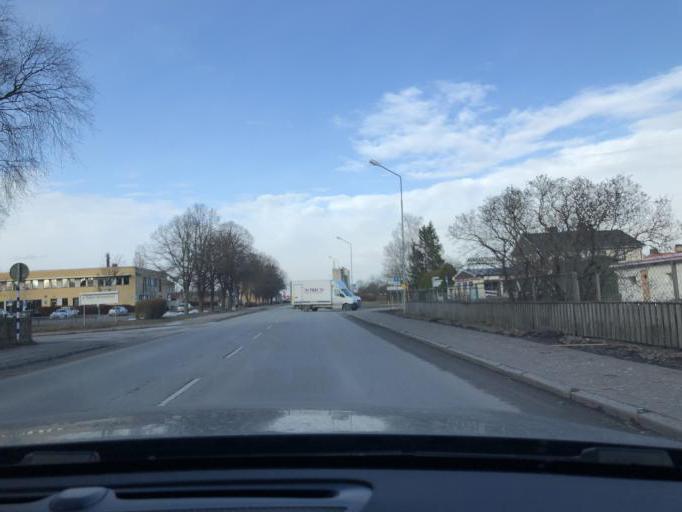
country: SE
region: Uppsala
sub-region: Tierps Kommun
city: Tierp
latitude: 60.3355
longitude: 17.5150
